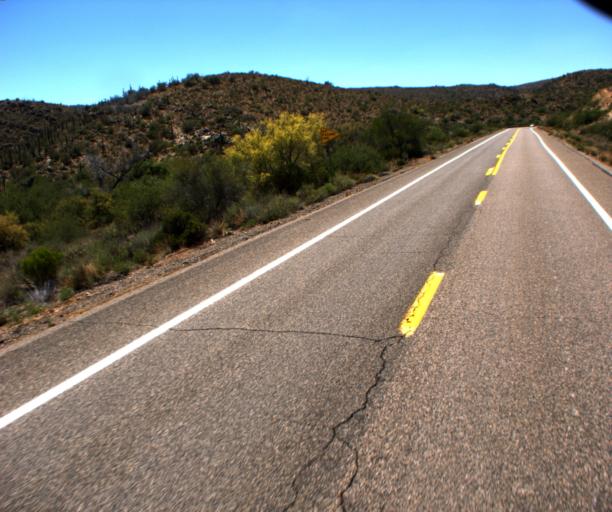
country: US
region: Arizona
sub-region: Yavapai County
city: Bagdad
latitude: 34.5165
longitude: -113.0835
